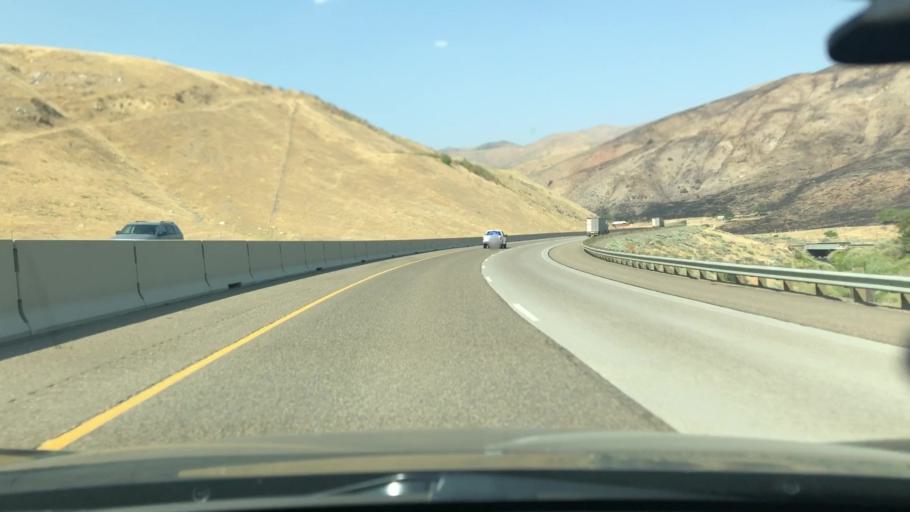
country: US
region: Idaho
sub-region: Washington County
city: Weiser
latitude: 44.4082
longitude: -117.3126
